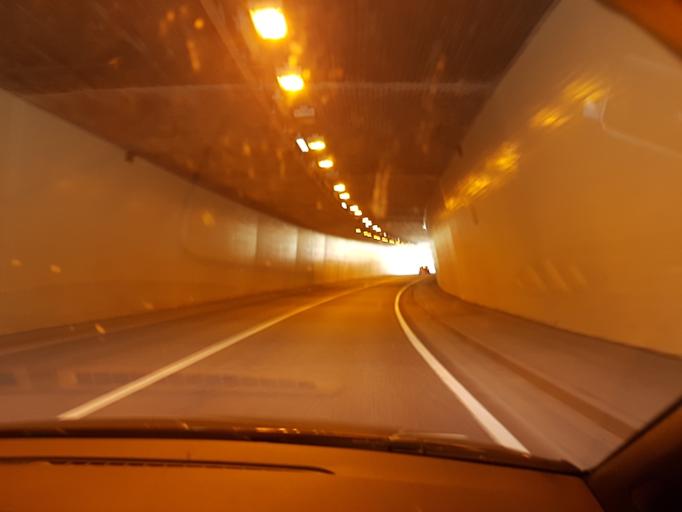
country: CH
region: Grisons
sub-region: Praettigau/Davos District
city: Klosters Serneus
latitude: 46.8880
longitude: 9.8536
